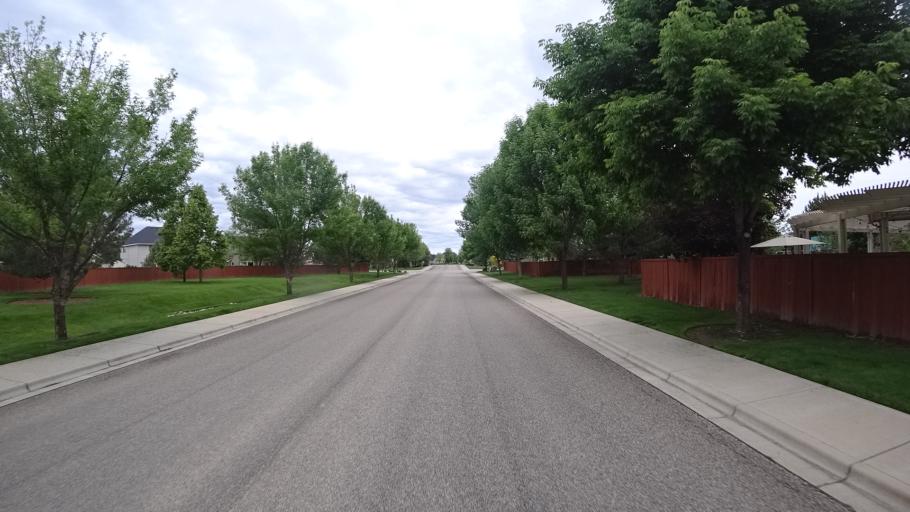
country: US
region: Idaho
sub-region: Ada County
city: Star
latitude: 43.6980
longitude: -116.4804
